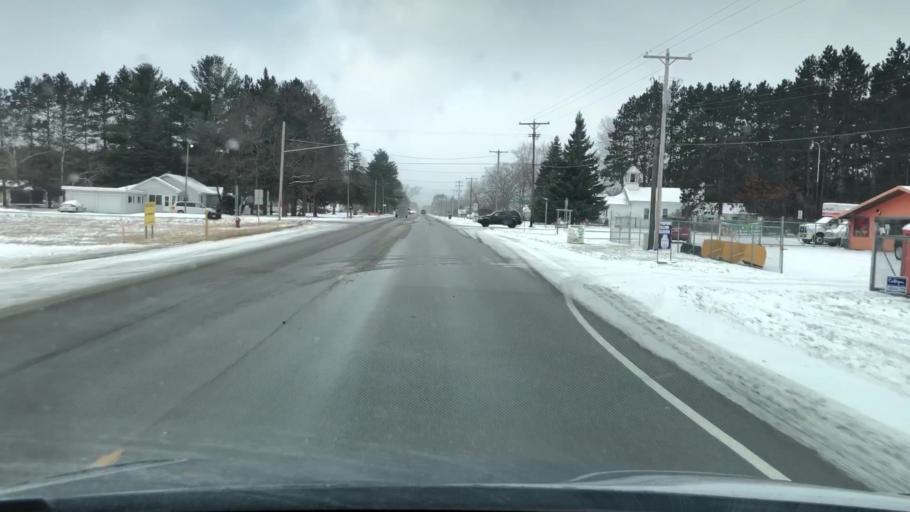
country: US
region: Michigan
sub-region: Wexford County
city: Cadillac
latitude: 44.2813
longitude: -85.4359
